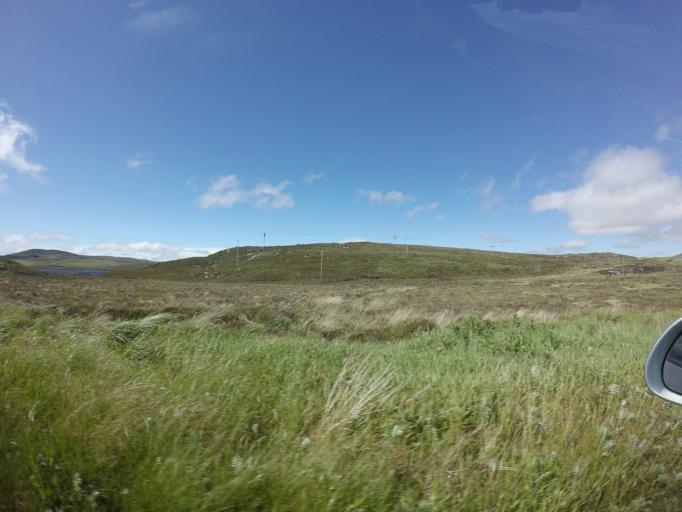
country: GB
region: Scotland
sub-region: Eilean Siar
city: Stornoway
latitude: 58.1202
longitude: -6.5108
